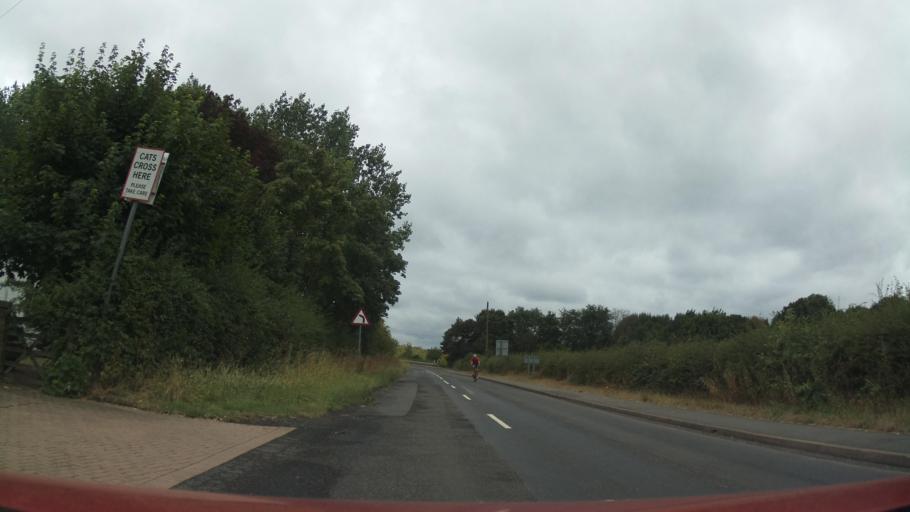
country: GB
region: England
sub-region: Derbyshire
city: Findern
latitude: 52.8623
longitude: -1.5501
